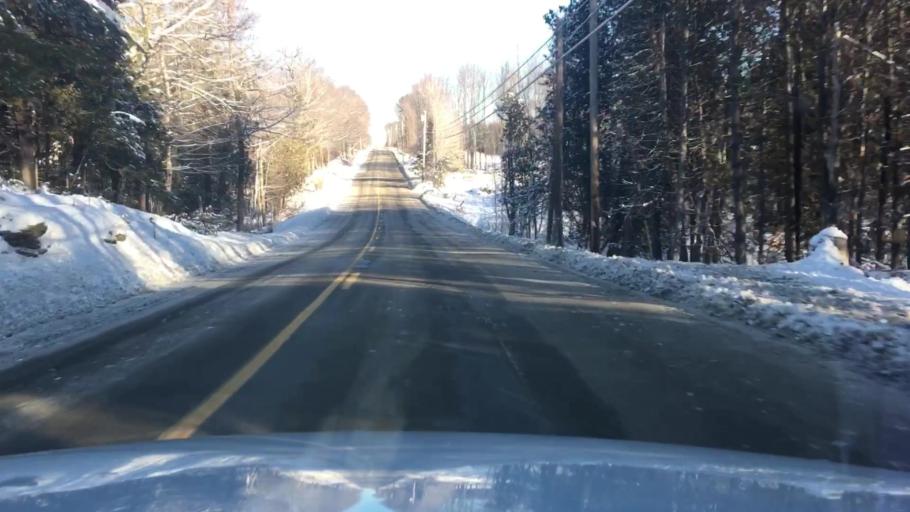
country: US
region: Maine
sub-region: Kennebec County
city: Mount Vernon
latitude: 44.4745
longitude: -69.9727
